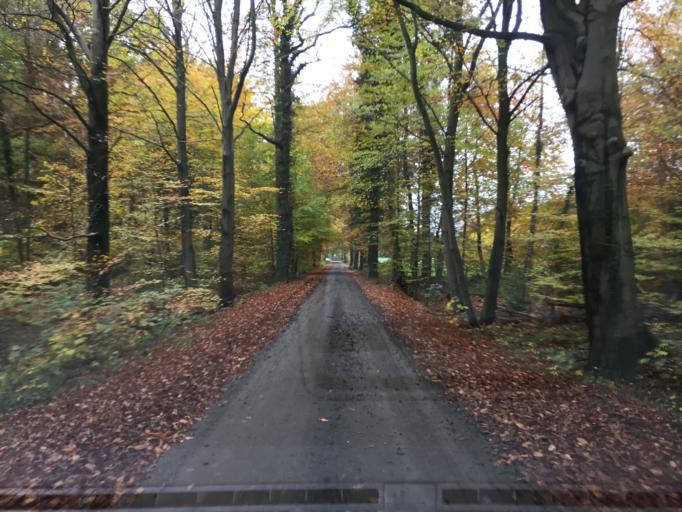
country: DE
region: Lower Saxony
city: Linsburg
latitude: 52.5773
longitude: 9.3159
